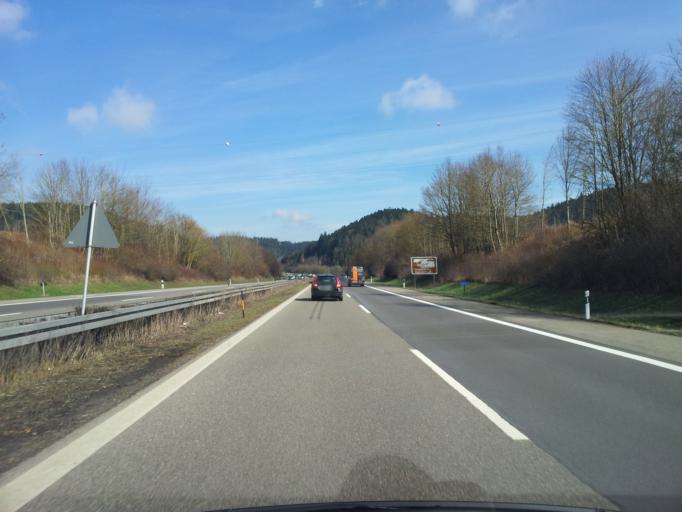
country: DE
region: Baden-Wuerttemberg
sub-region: Freiburg Region
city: Epfendorf
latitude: 48.2753
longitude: 8.6395
